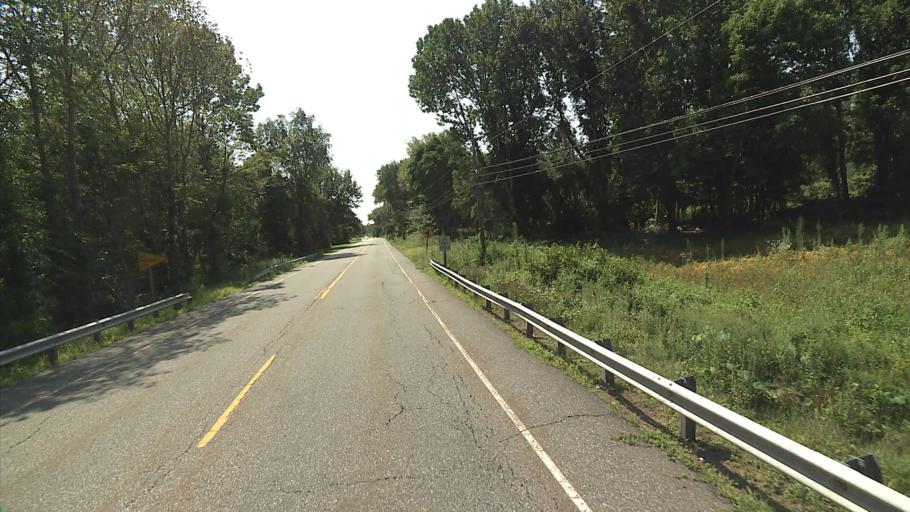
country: US
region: Connecticut
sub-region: New London County
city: Colchester
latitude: 41.5193
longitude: -72.2557
